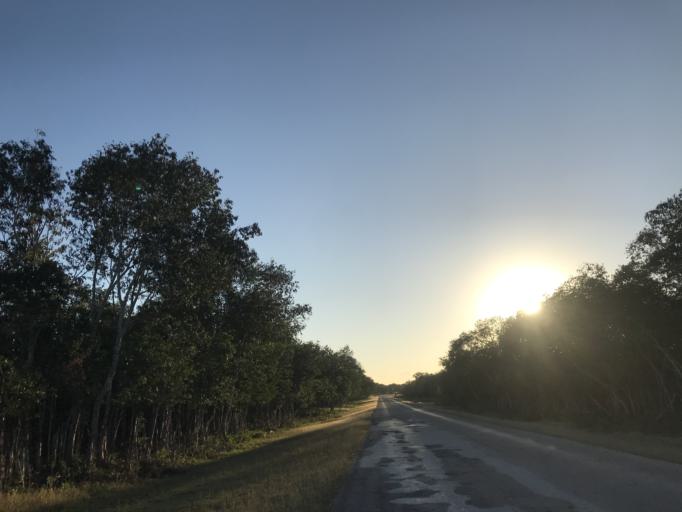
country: CU
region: Cienfuegos
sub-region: Municipio de Aguada de Pasajeros
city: Aguada de Pasajeros
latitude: 22.0696
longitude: -81.0385
